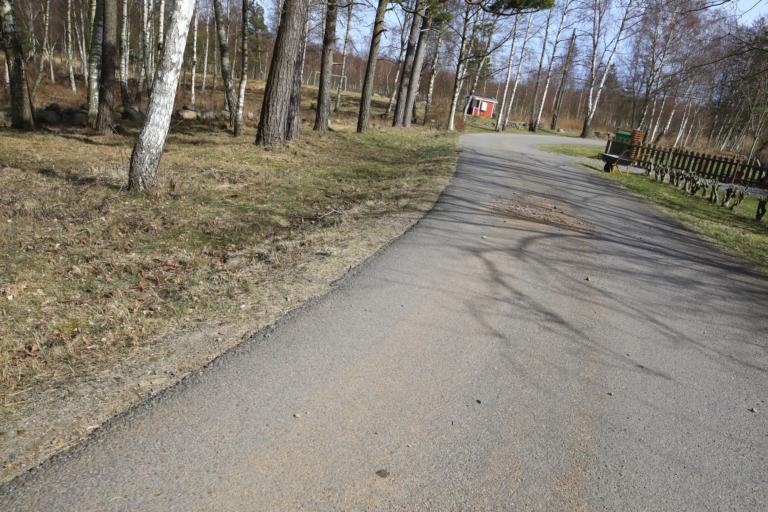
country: SE
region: Halland
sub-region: Kungsbacka Kommun
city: Frillesas
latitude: 57.2687
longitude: 12.1204
